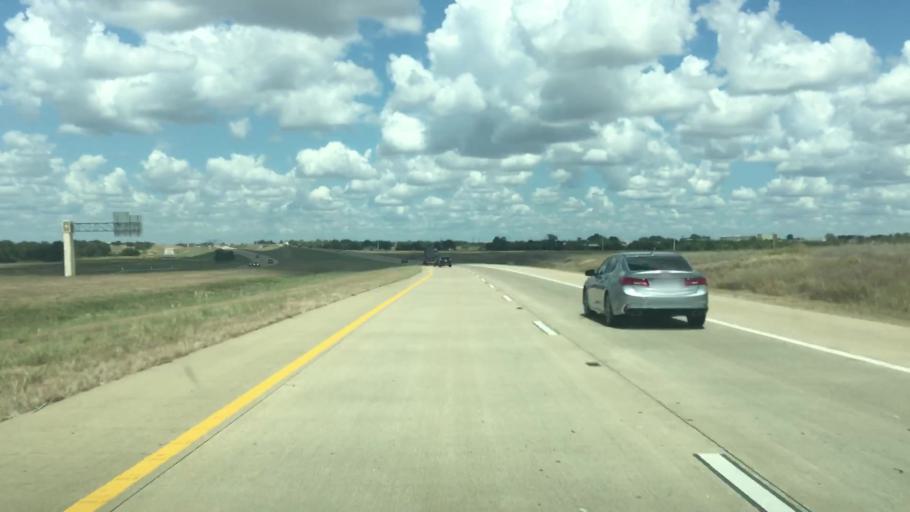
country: US
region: Texas
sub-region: Williamson County
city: Hutto
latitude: 30.5540
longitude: -97.5767
